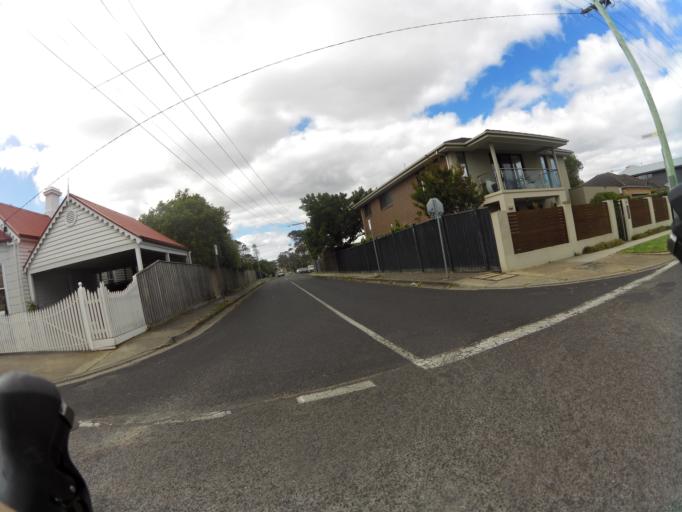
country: AU
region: Victoria
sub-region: Mornington Peninsula
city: Mornington
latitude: -38.2263
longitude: 145.0393
